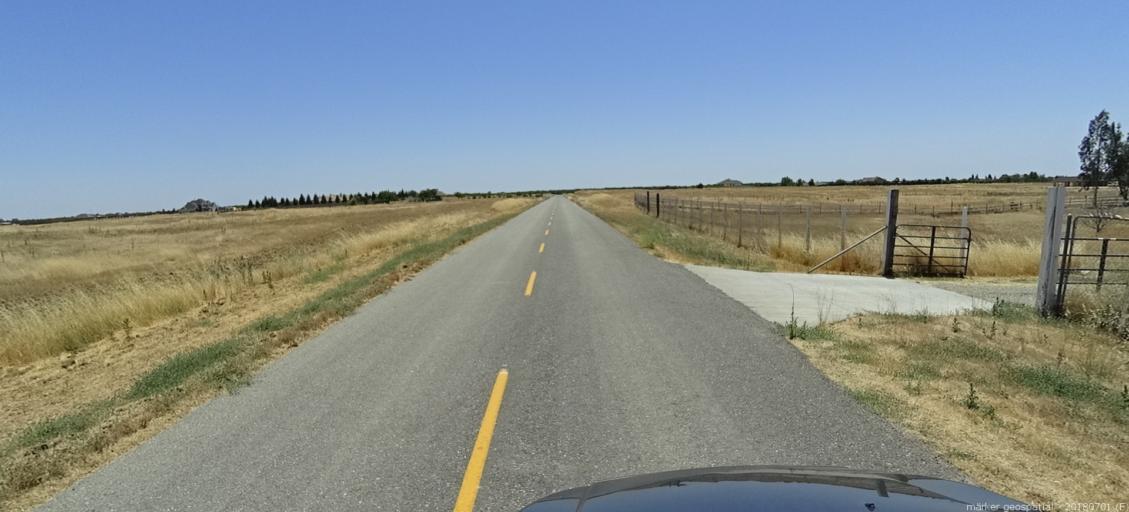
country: US
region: California
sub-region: Madera County
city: Madera Acres
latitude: 37.0604
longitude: -120.0181
